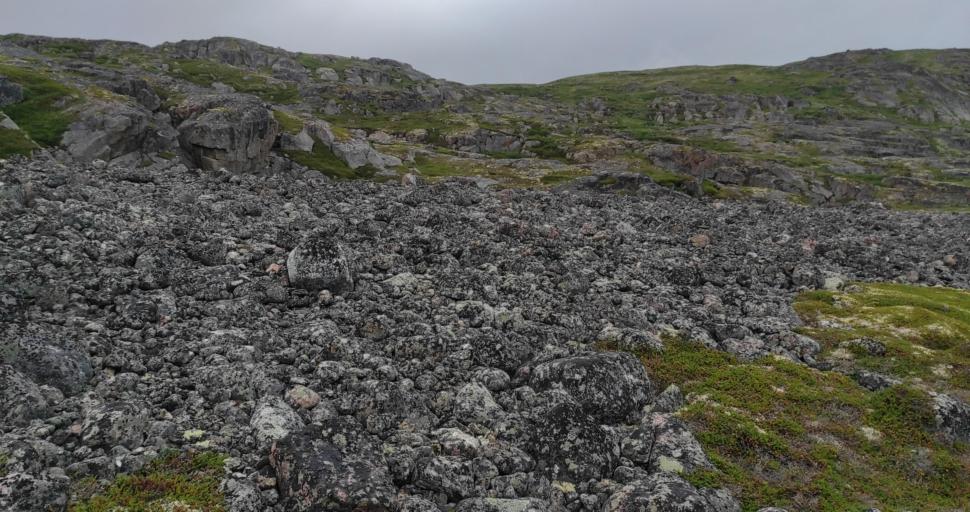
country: RU
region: Murmansk
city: Teriberka
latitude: 69.2139
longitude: 35.5405
